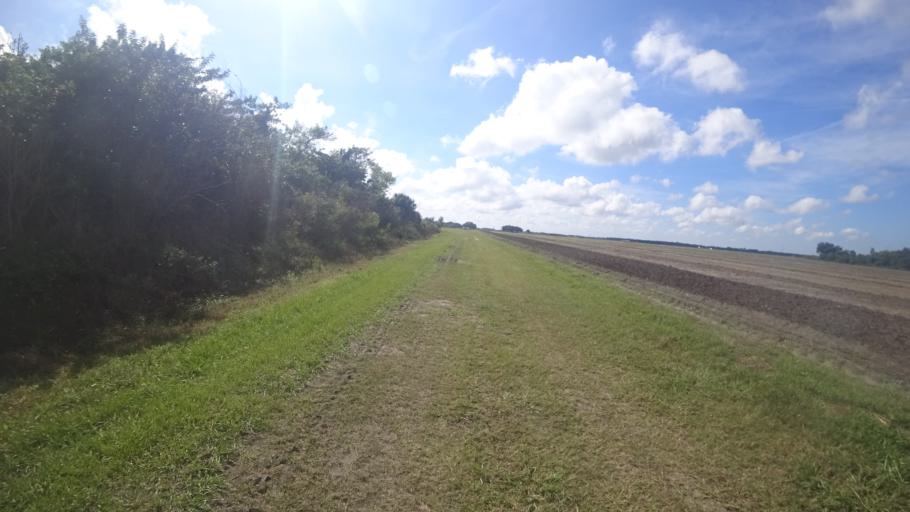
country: US
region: Florida
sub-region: Hillsborough County
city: Ruskin
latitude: 27.6388
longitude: -82.4972
